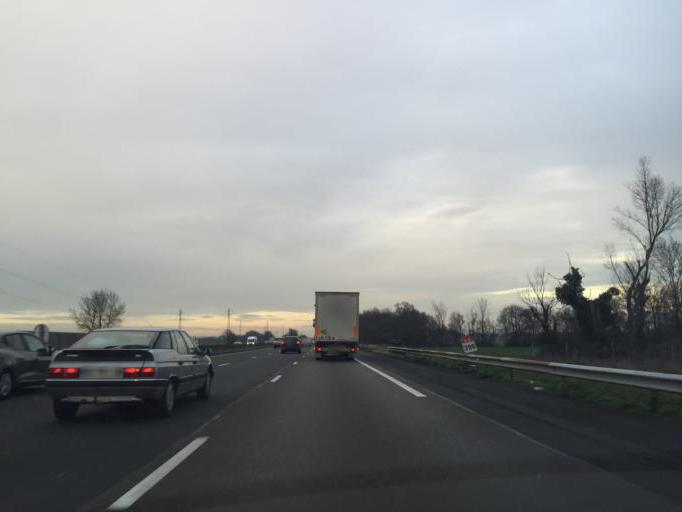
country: FR
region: Bourgogne
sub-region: Departement de Saone-et-Loire
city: Creches-sur-Saone
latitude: 46.2259
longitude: 4.7915
